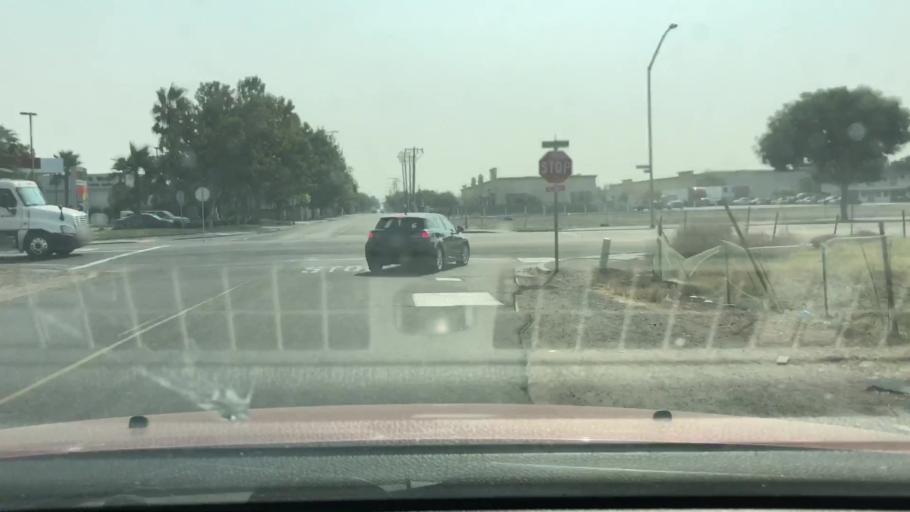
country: US
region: California
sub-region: San Joaquin County
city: Tracy
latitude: 37.7650
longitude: -121.4355
